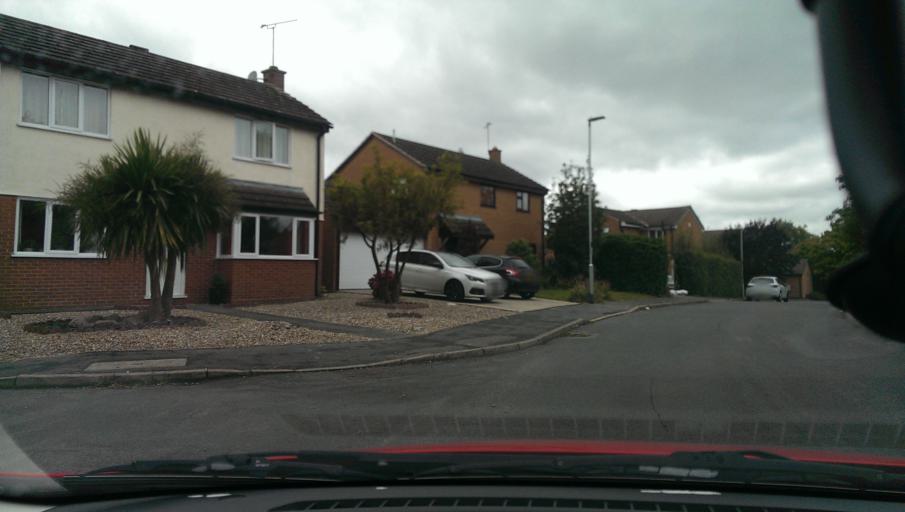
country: GB
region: England
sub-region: Leicestershire
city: Narborough
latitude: 52.5685
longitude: -1.2001
